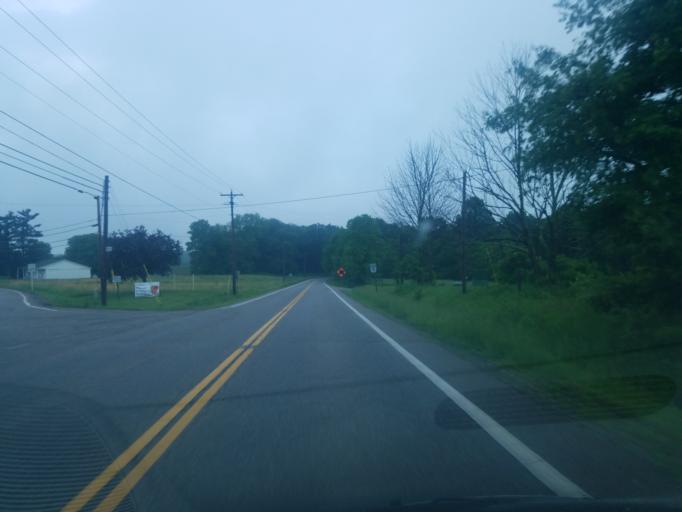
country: US
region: Ohio
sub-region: Columbiana County
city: Salem
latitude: 40.8446
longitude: -80.8958
